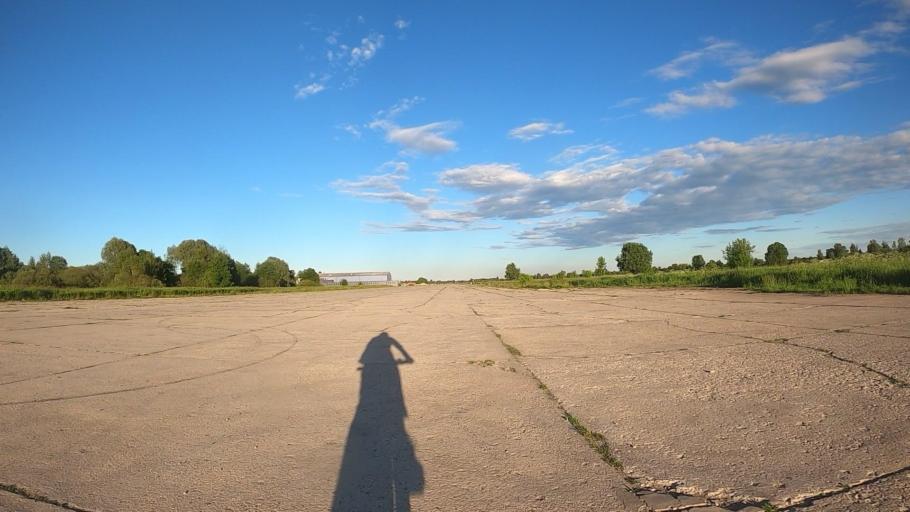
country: LV
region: Kekava
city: Kekava
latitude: 56.8875
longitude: 24.2152
